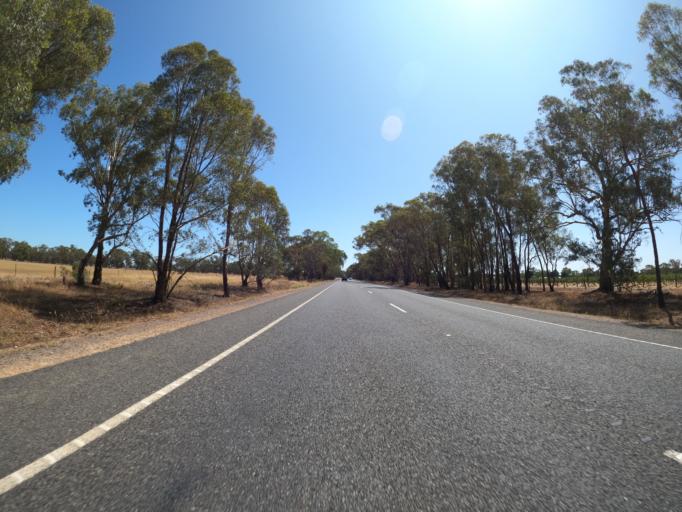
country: AU
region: New South Wales
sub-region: Corowa Shire
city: Corowa
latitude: -36.0626
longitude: 146.4011
